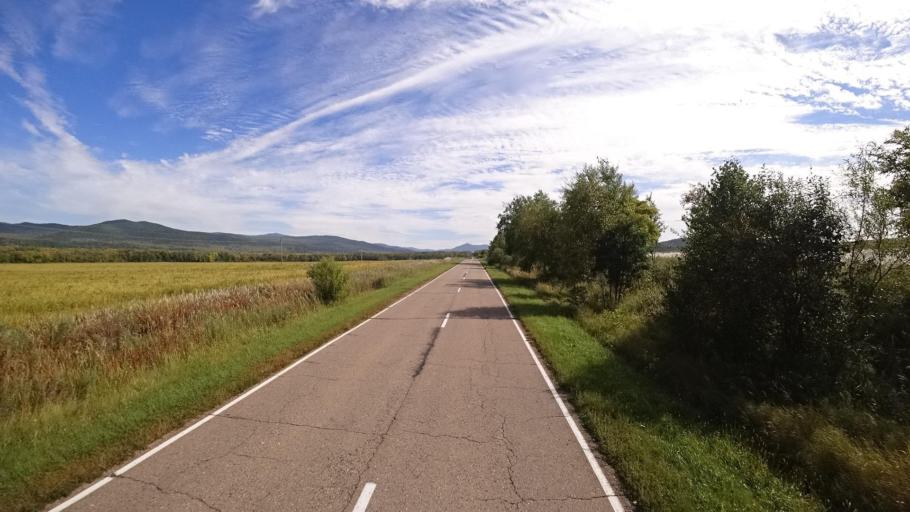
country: RU
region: Primorskiy
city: Yakovlevka
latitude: 44.4167
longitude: 133.5828
